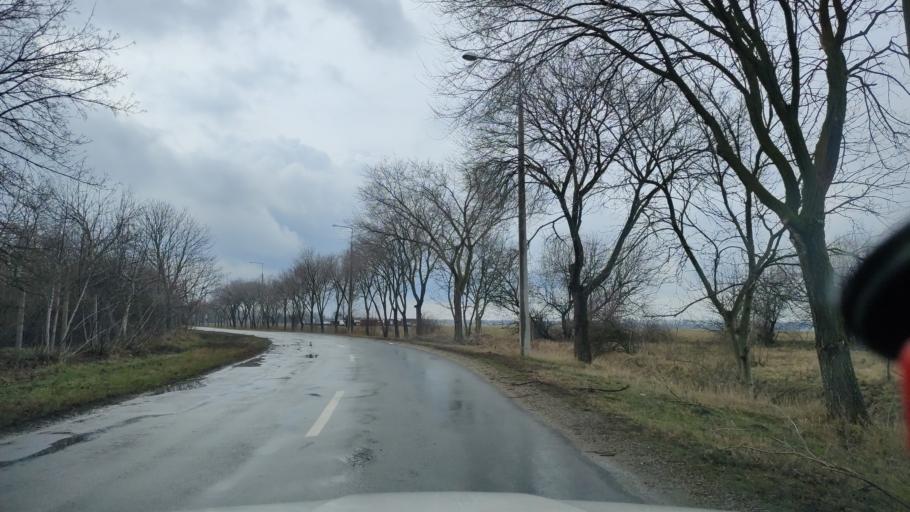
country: HU
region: Hajdu-Bihar
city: Hajduszoboszlo
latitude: 47.4601
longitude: 21.3991
